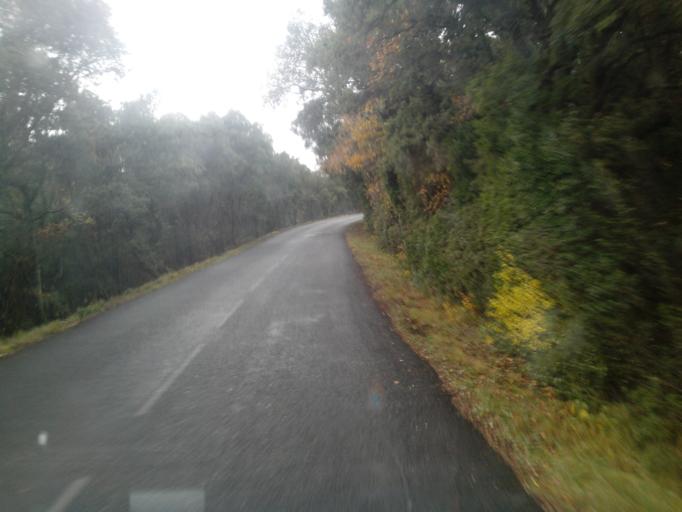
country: FR
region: Languedoc-Roussillon
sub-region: Departement de l'Herault
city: Saint-Martin-de-Londres
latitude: 43.8229
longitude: 3.6773
